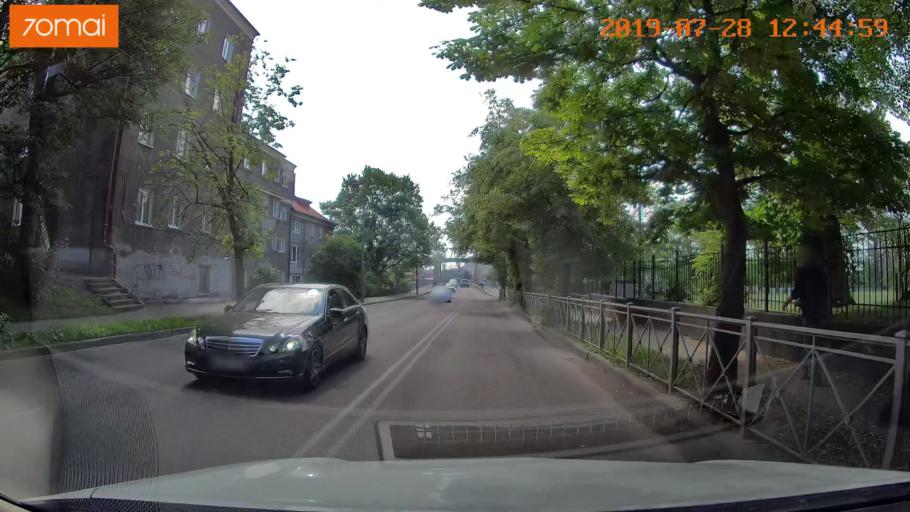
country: RU
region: Kaliningrad
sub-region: Gorod Kaliningrad
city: Kaliningrad
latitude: 54.7117
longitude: 20.4583
